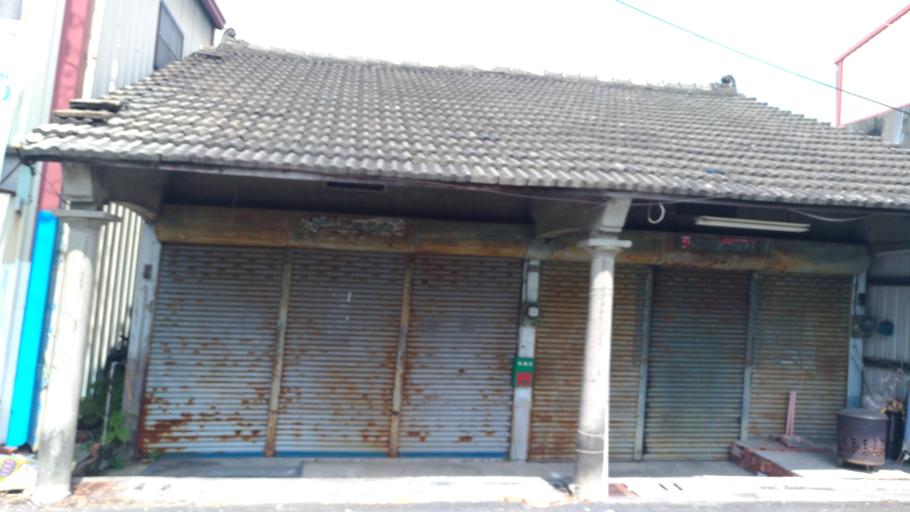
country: TW
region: Taiwan
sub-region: Yunlin
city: Douliu
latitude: 23.7555
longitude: 120.4971
